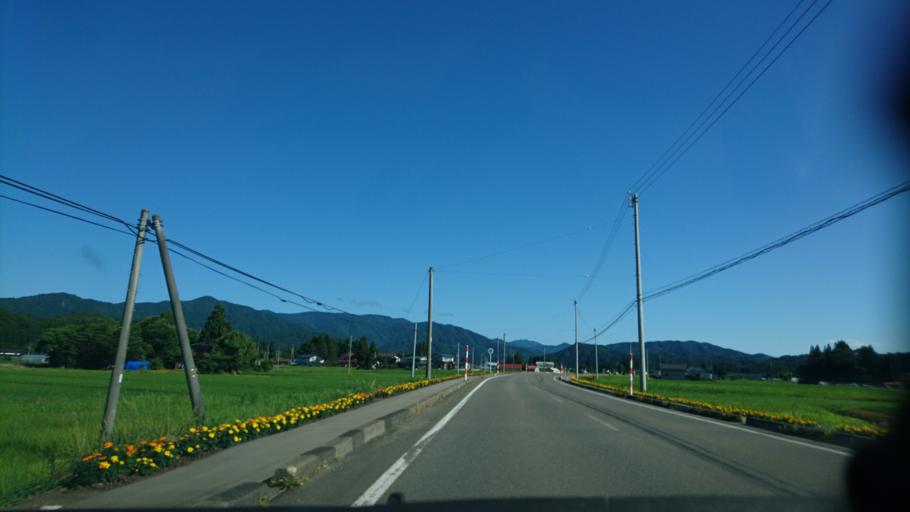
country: JP
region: Akita
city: Kakunodatemachi
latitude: 39.6437
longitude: 140.5707
